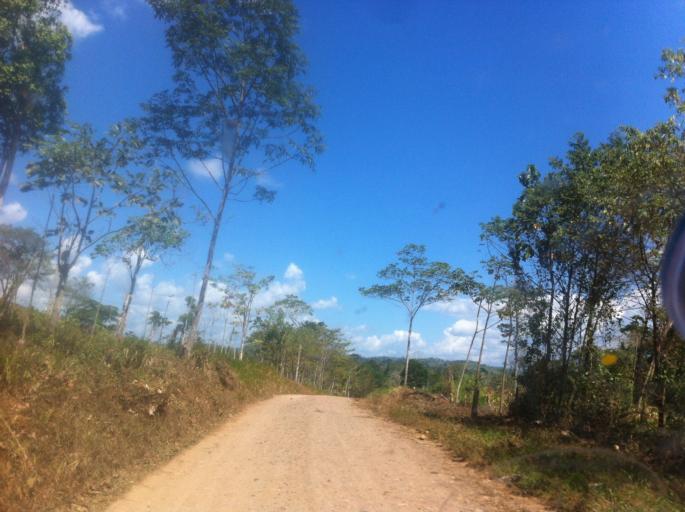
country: CR
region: Alajuela
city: Los Chiles
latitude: 11.2473
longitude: -84.4646
